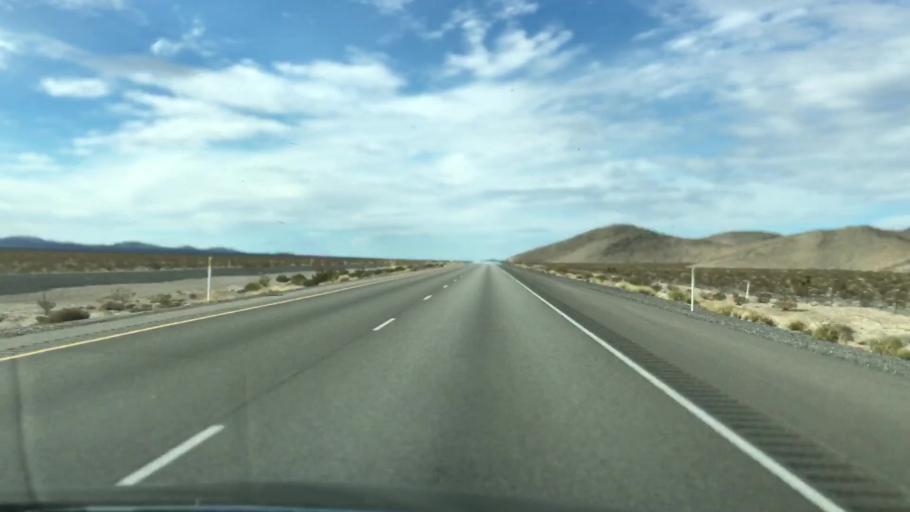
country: US
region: Nevada
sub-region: Nye County
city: Pahrump
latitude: 36.5707
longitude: -115.8429
